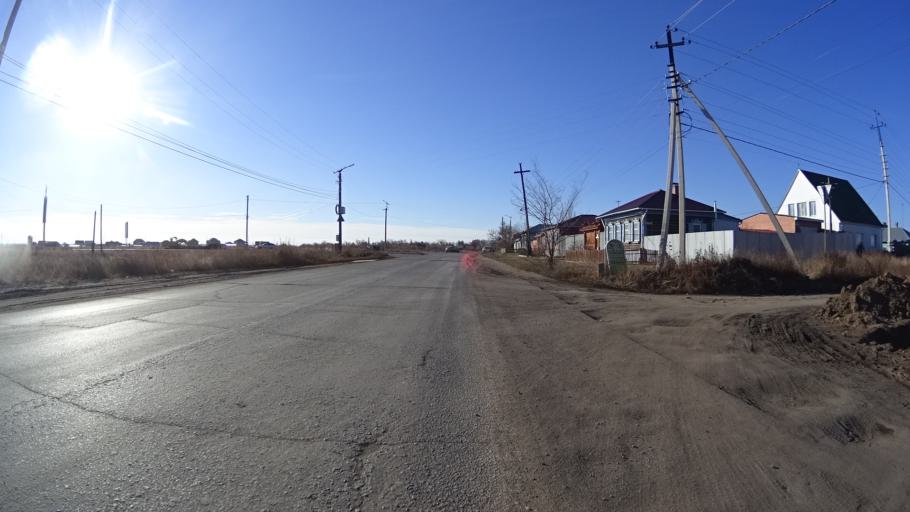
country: RU
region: Chelyabinsk
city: Troitsk
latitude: 54.0831
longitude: 61.5178
